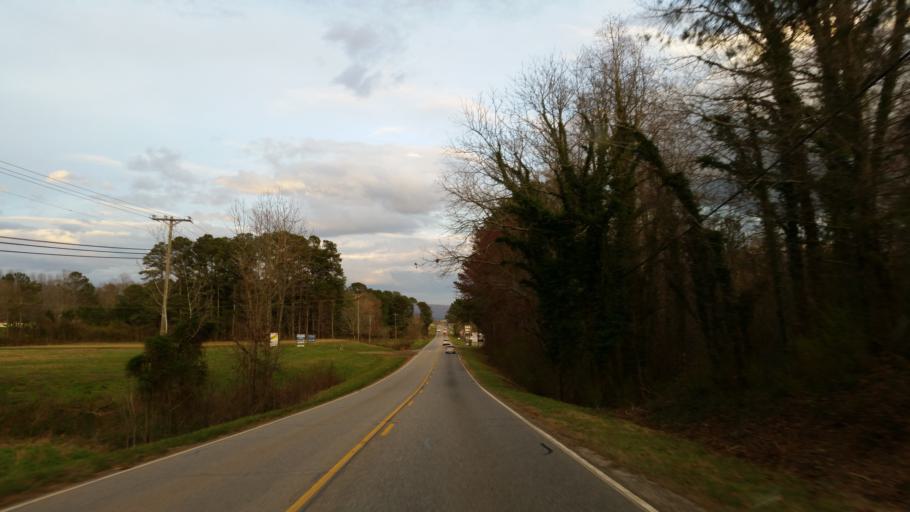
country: US
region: Georgia
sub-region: Pickens County
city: Jasper
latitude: 34.4648
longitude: -84.4705
